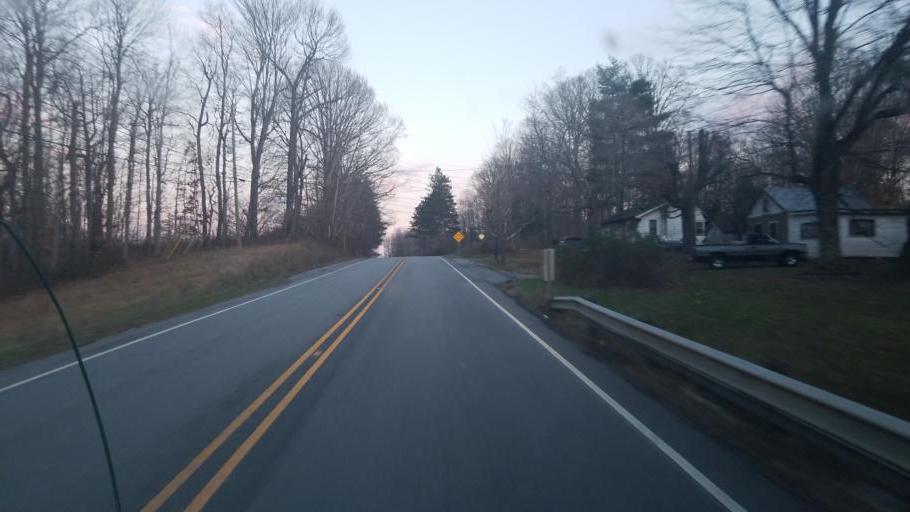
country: US
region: Indiana
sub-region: Lawrence County
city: Bedford
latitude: 38.8747
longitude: -86.2966
